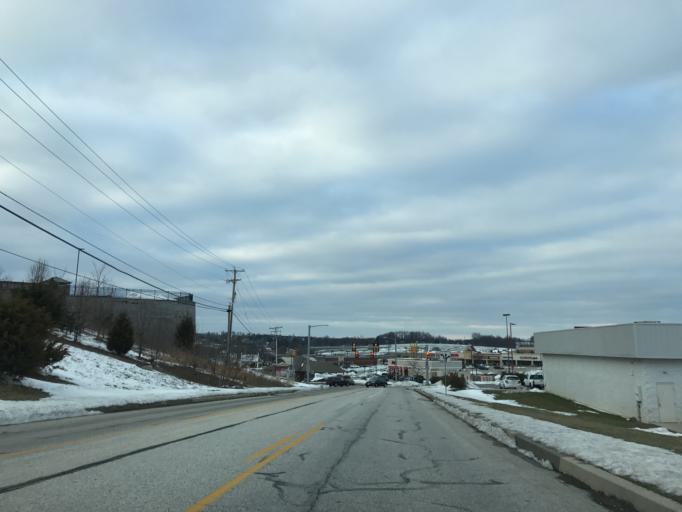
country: US
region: Pennsylvania
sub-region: York County
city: Shrewsbury
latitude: 39.7678
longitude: -76.6713
